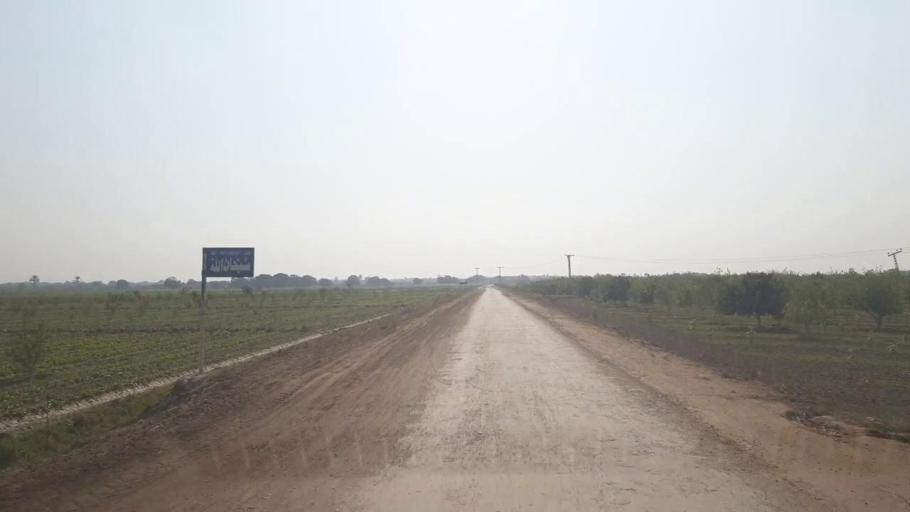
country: PK
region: Sindh
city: Tando Allahyar
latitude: 25.4615
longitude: 68.8147
